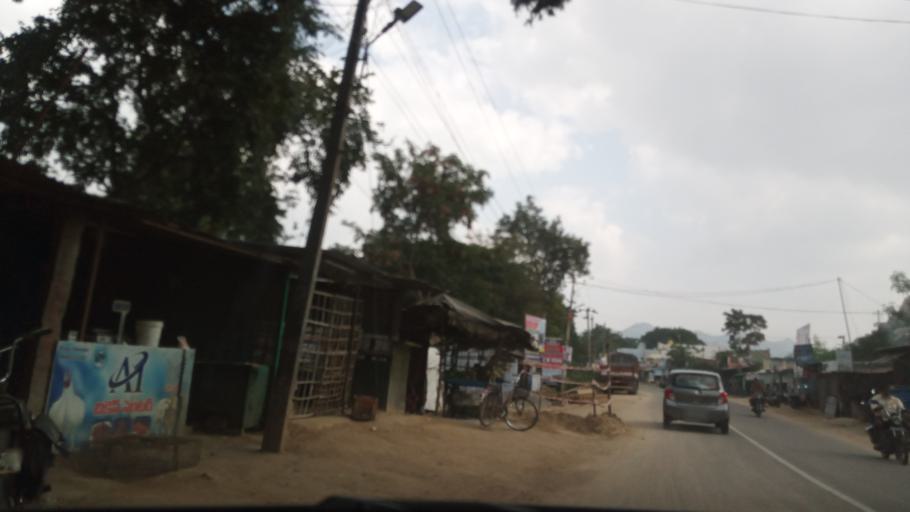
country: IN
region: Andhra Pradesh
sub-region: Chittoor
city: Madanapalle
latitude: 13.6441
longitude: 78.5661
